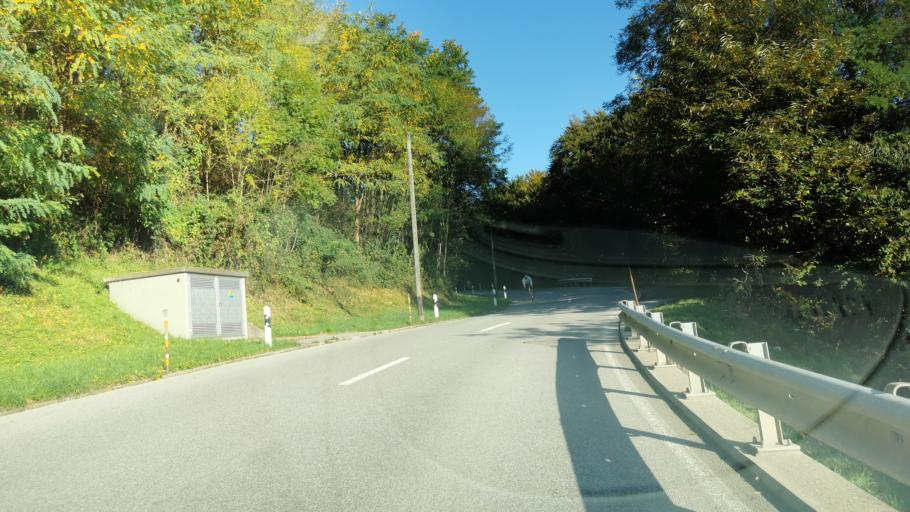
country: CH
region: Ticino
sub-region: Lugano District
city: Pura
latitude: 45.9940
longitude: 8.8651
